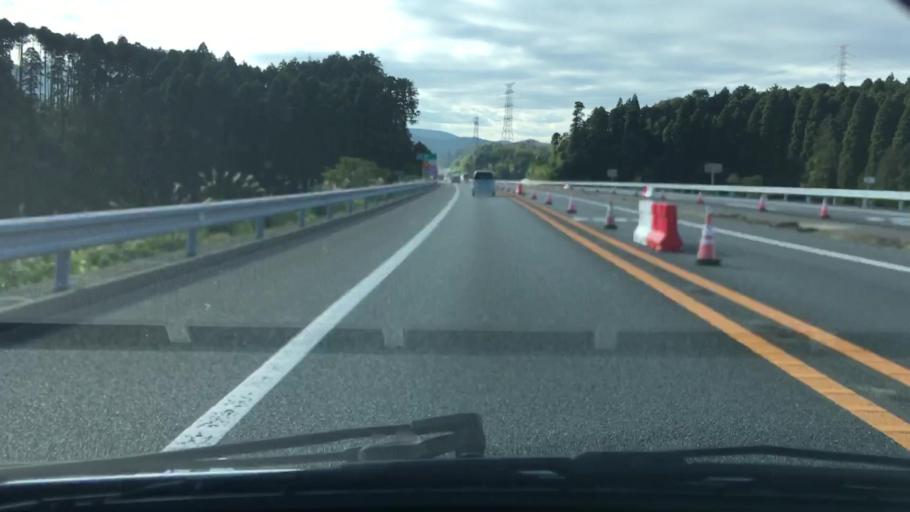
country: JP
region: Chiba
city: Kimitsu
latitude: 35.2901
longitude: 139.9298
